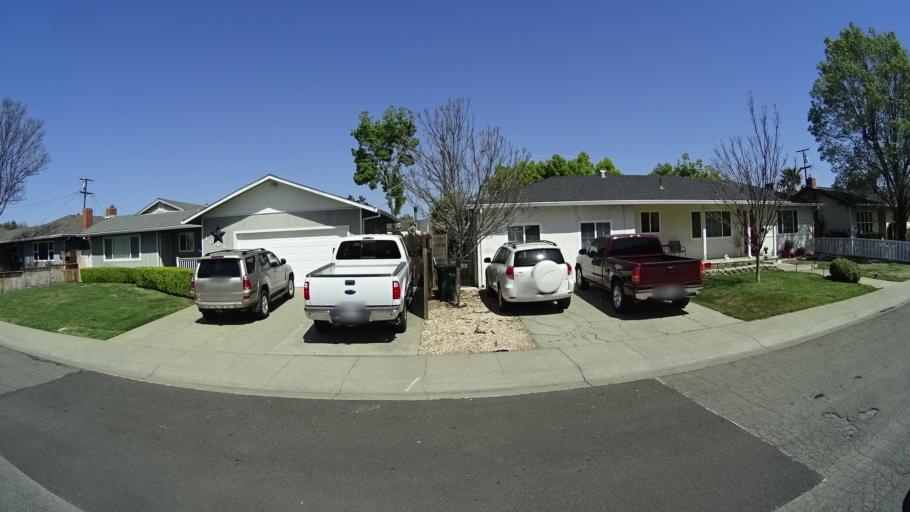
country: US
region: California
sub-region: Glenn County
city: Willows
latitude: 39.5134
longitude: -122.2070
